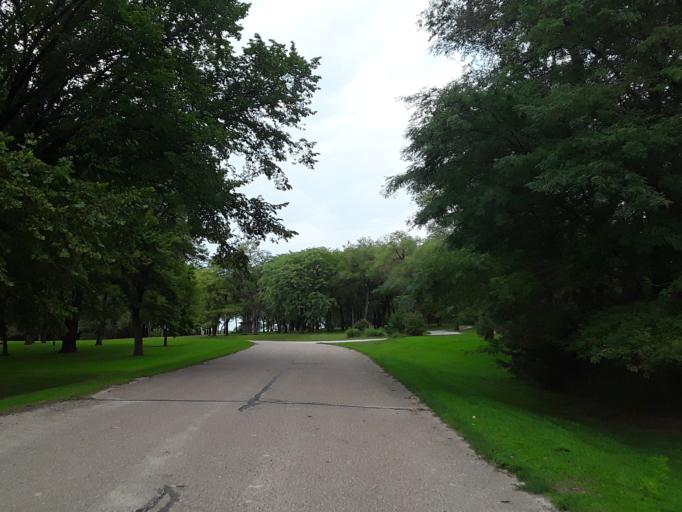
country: US
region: Nebraska
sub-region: Saunders County
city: Ashland
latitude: 41.1007
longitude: -96.4361
